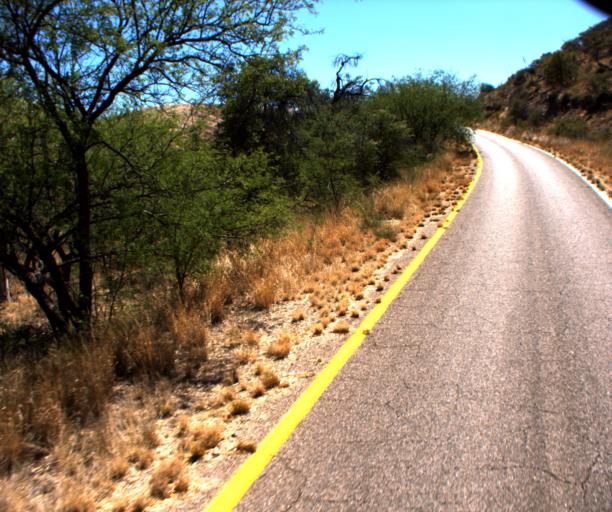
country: US
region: Arizona
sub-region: Santa Cruz County
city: Rio Rico
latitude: 31.3856
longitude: -111.0581
